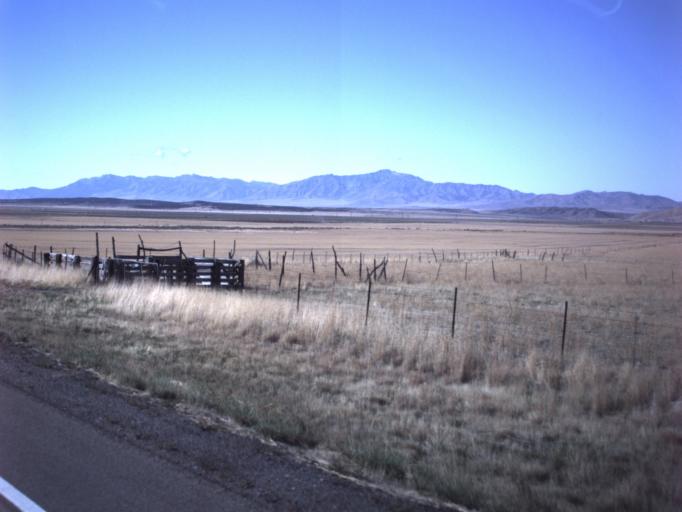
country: US
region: Utah
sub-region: Juab County
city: Nephi
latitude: 39.4963
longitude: -111.8788
